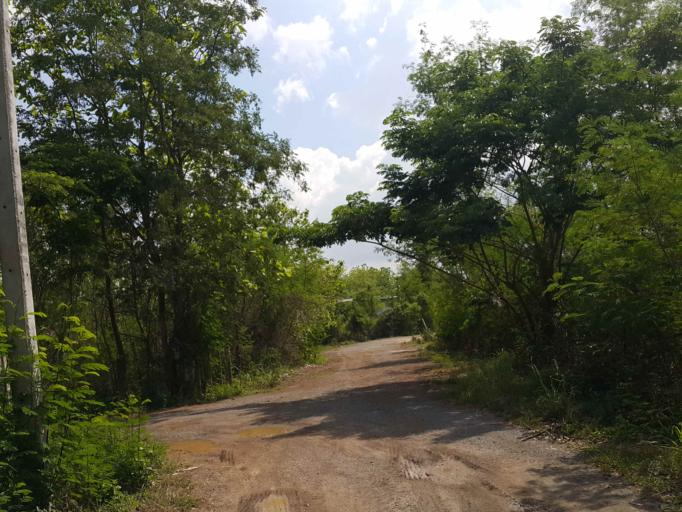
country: TH
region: Chiang Mai
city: San Kamphaeng
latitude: 18.7658
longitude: 99.0685
